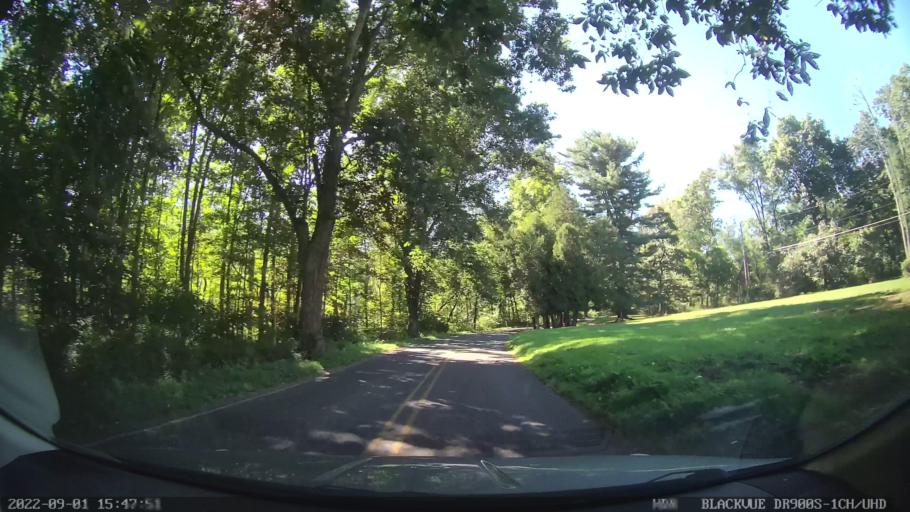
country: US
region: Pennsylvania
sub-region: Berks County
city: Topton
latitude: 40.4711
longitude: -75.7241
